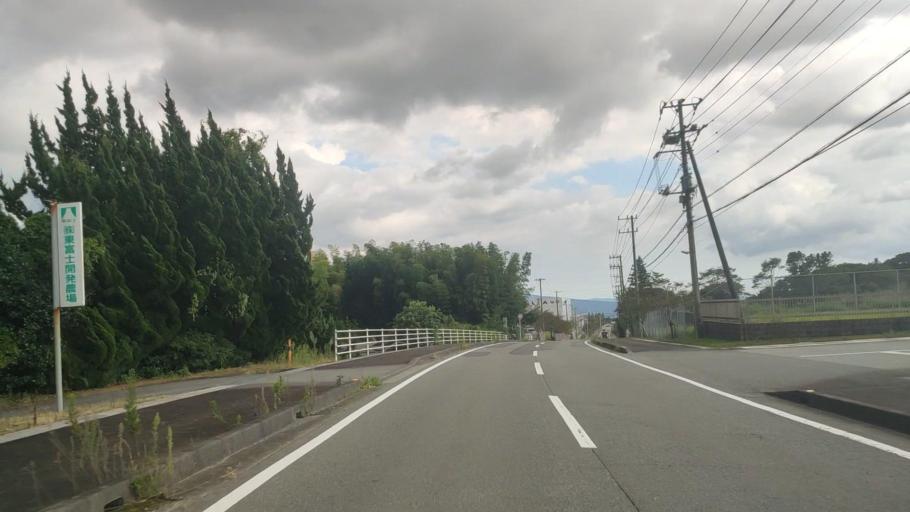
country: JP
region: Shizuoka
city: Gotemba
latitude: 35.2754
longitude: 138.8924
